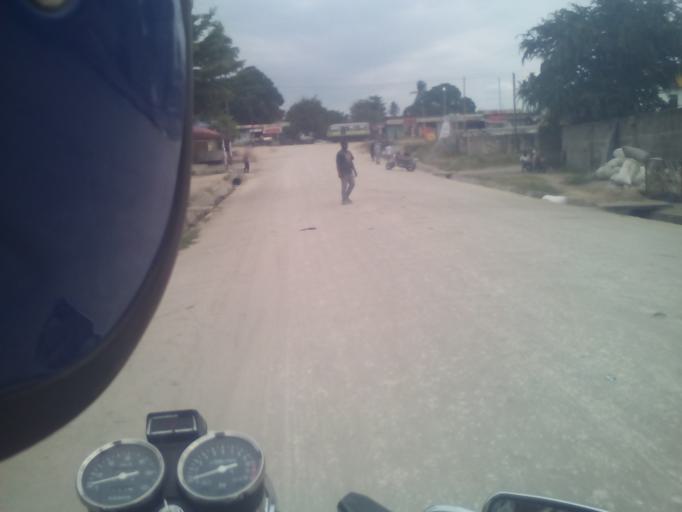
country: TZ
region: Dar es Salaam
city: Dar es Salaam
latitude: -6.8745
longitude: 39.2251
